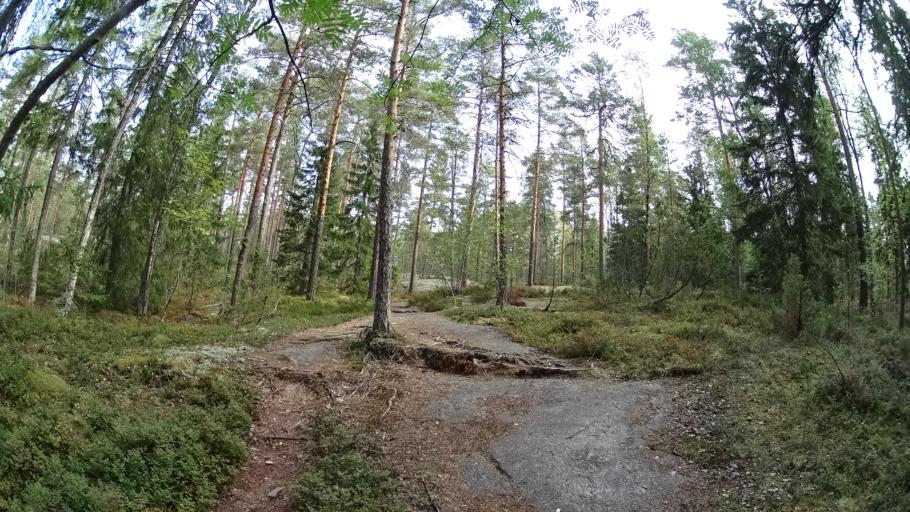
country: FI
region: Uusimaa
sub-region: Helsinki
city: Espoo
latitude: 60.2960
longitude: 24.5797
